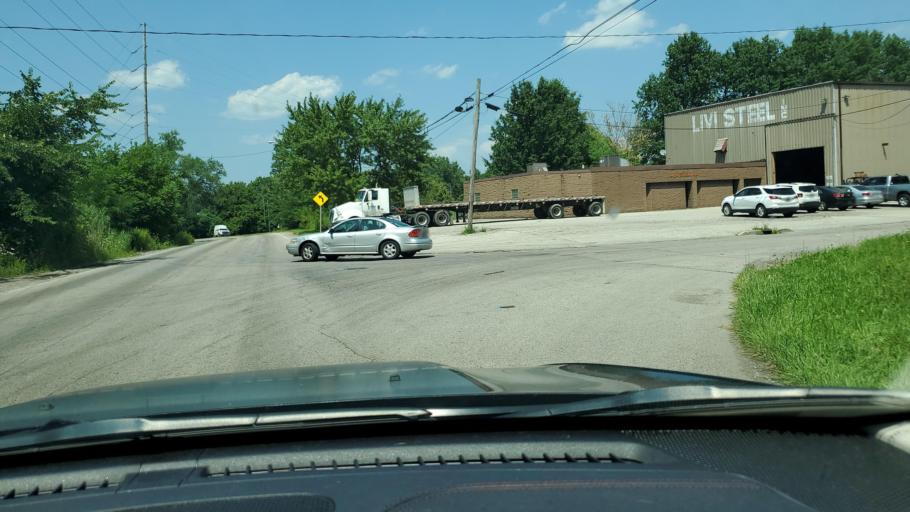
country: US
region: Ohio
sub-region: Trumbull County
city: Warren
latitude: 41.2195
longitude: -80.8058
